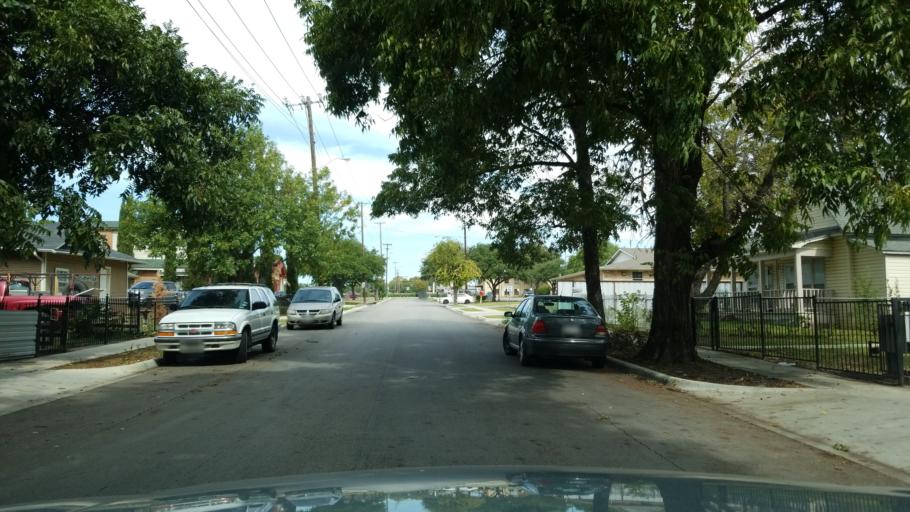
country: US
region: Texas
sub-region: Dallas County
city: Dallas
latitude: 32.7891
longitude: -96.7444
